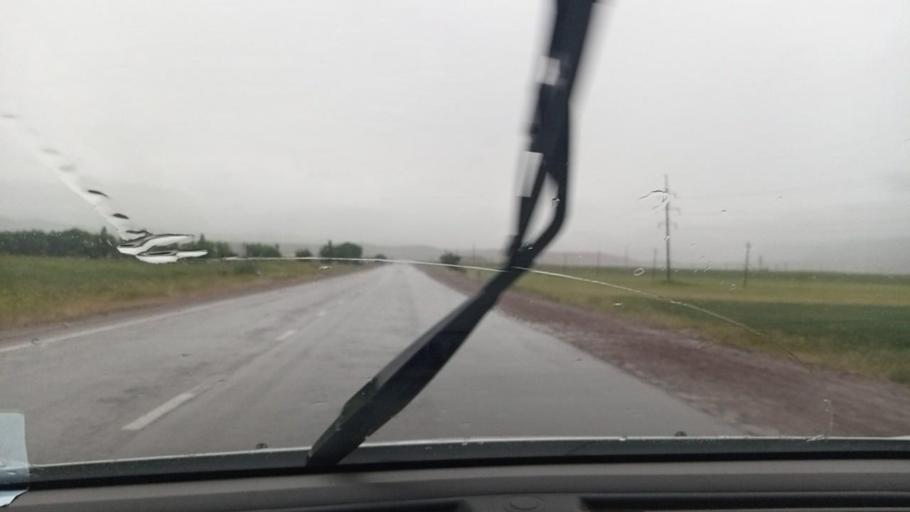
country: UZ
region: Toshkent
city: Angren
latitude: 41.0376
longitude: 70.1469
